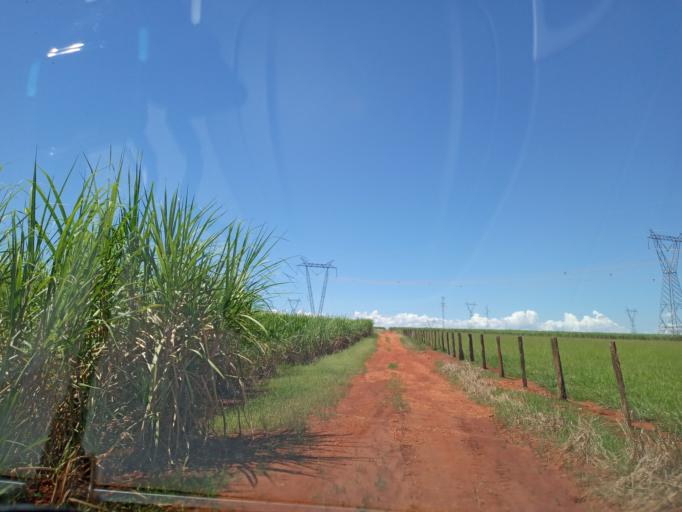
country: BR
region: Goias
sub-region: Itumbiara
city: Itumbiara
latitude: -18.3956
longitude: -49.1233
